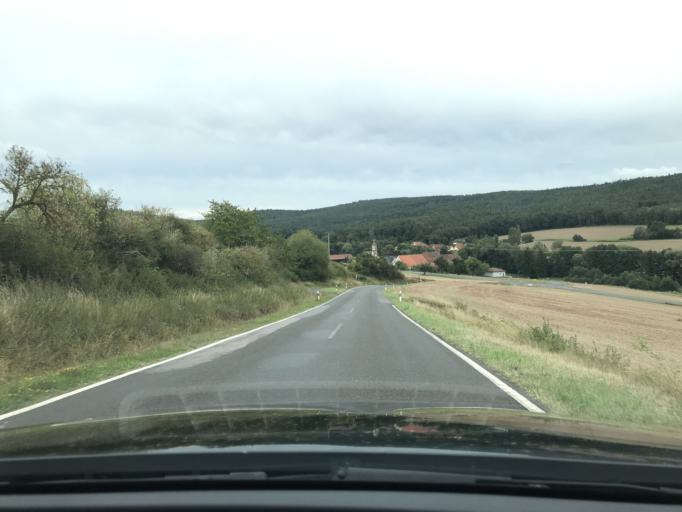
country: DE
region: Bavaria
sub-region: Regierungsbezirk Unterfranken
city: Burgpreppach
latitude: 50.1071
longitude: 10.6847
